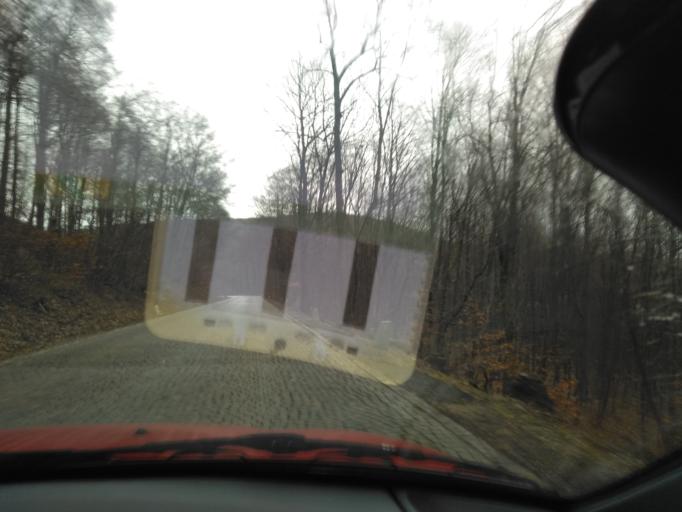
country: AT
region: Lower Austria
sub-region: Politischer Bezirk Wien-Umgebung
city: Klosterneuburg
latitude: 48.2695
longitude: 16.3040
